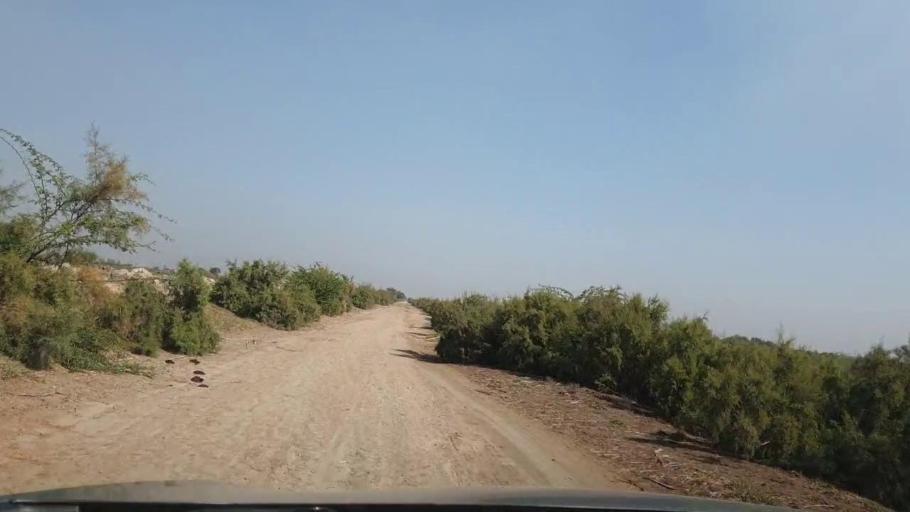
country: PK
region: Sindh
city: Berani
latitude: 25.6575
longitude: 68.8823
